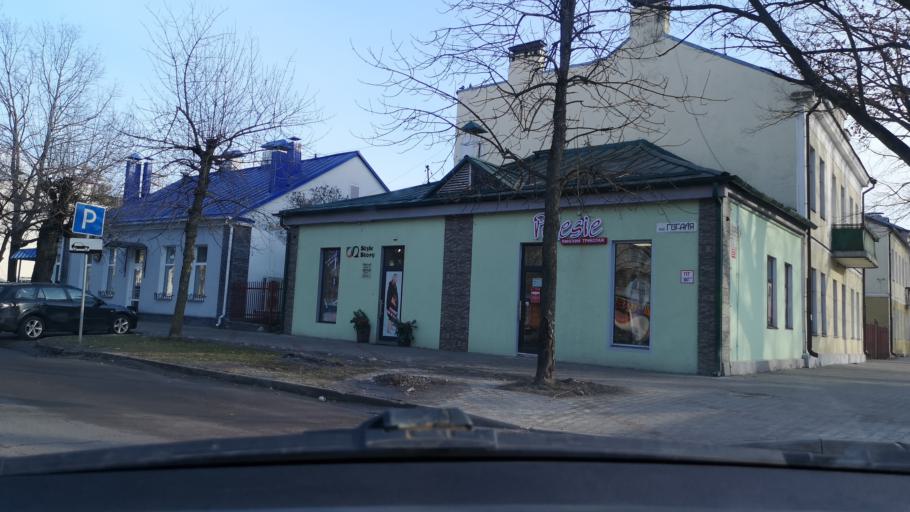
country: BY
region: Brest
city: Brest
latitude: 52.0924
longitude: 23.6914
